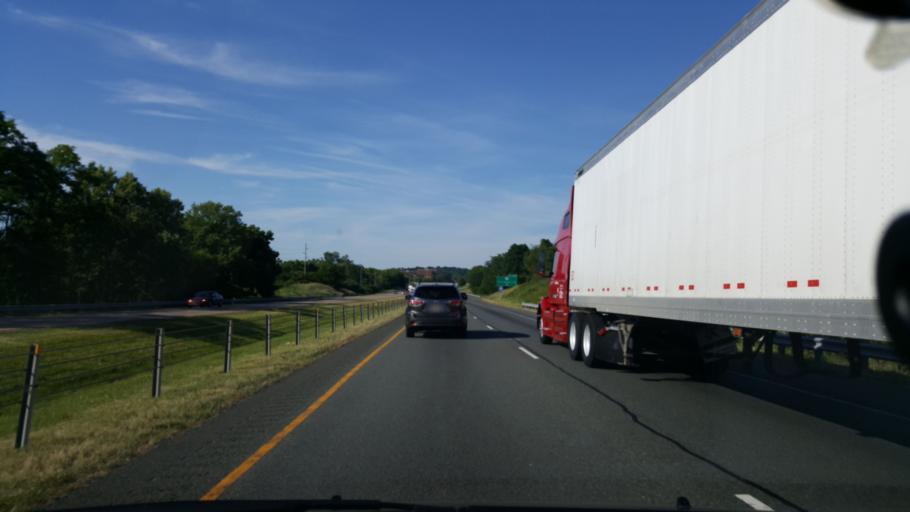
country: US
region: Virginia
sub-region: City of Harrisonburg
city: Harrisonburg
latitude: 38.4217
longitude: -78.8811
